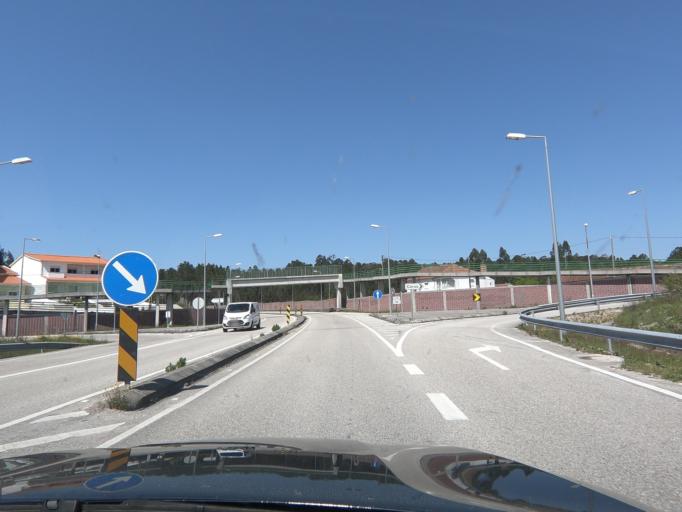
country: PT
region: Coimbra
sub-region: Miranda do Corvo
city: Miranda do Corvo
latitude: 40.0911
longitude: -8.3160
